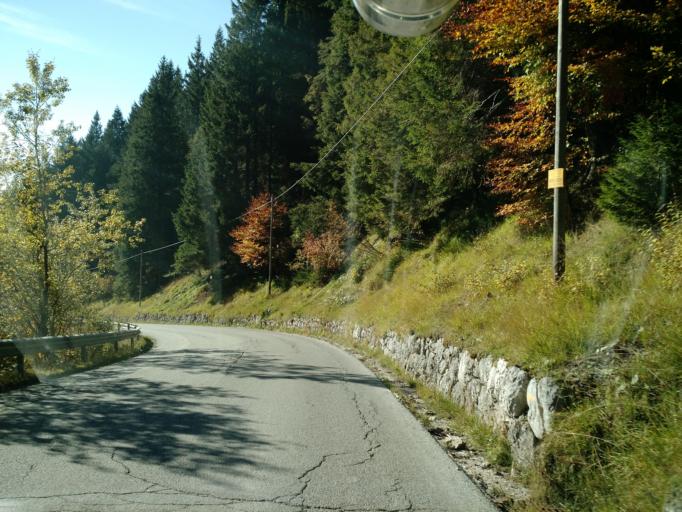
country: IT
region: Veneto
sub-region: Provincia di Vicenza
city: Gallio
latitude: 45.9118
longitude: 11.5679
